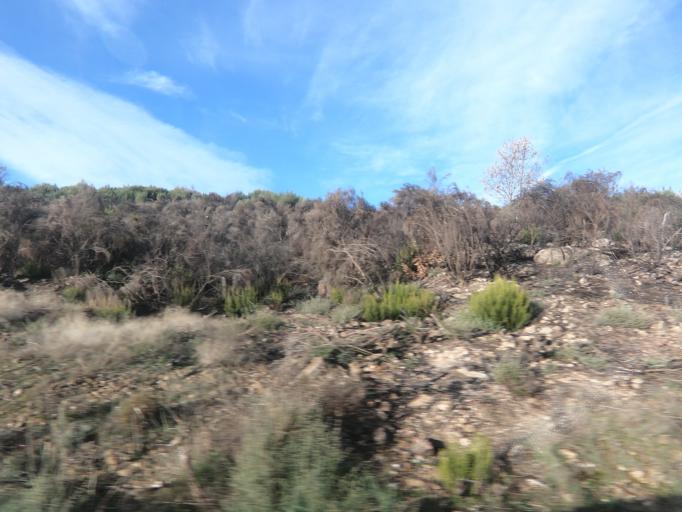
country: PT
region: Vila Real
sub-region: Sabrosa
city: Sabrosa
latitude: 41.3040
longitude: -7.6024
